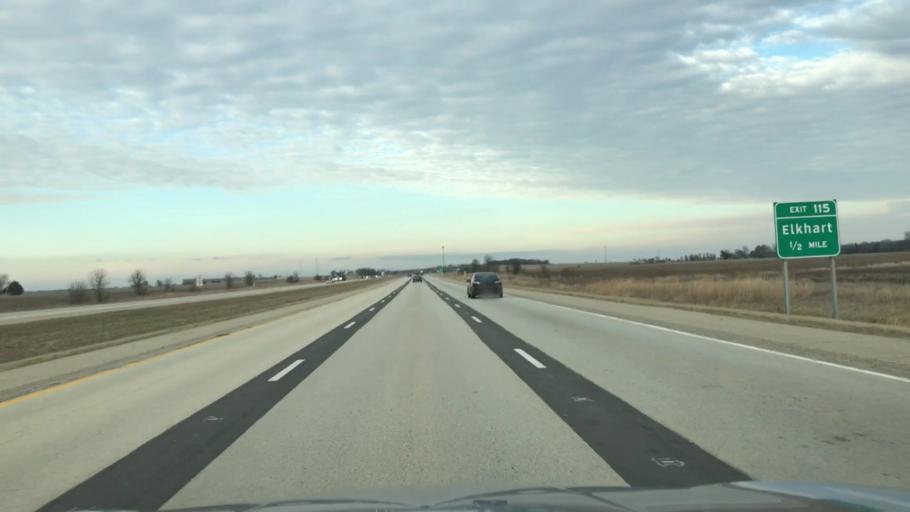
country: US
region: Illinois
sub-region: Sangamon County
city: Williamsville
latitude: 40.0091
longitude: -89.5001
